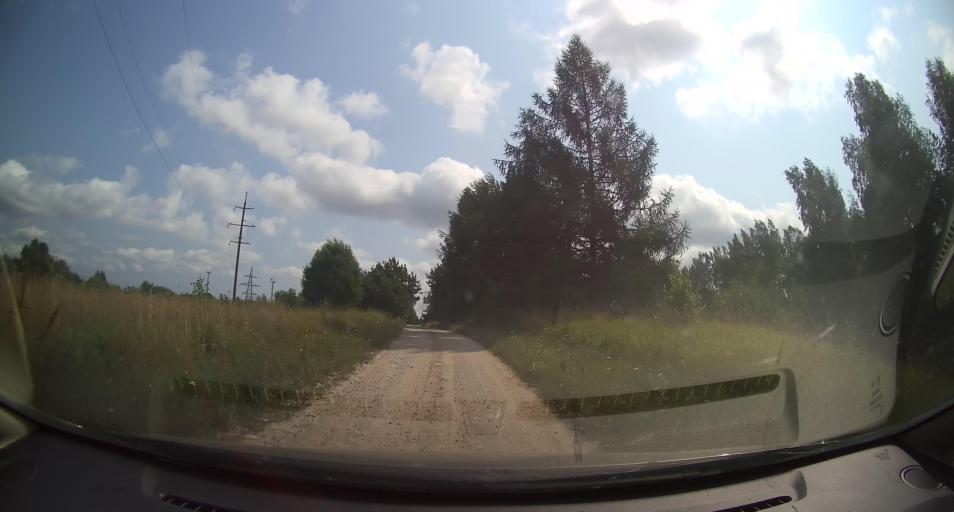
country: EE
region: Paernumaa
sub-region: Audru vald
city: Audru
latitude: 58.5151
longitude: 24.3619
